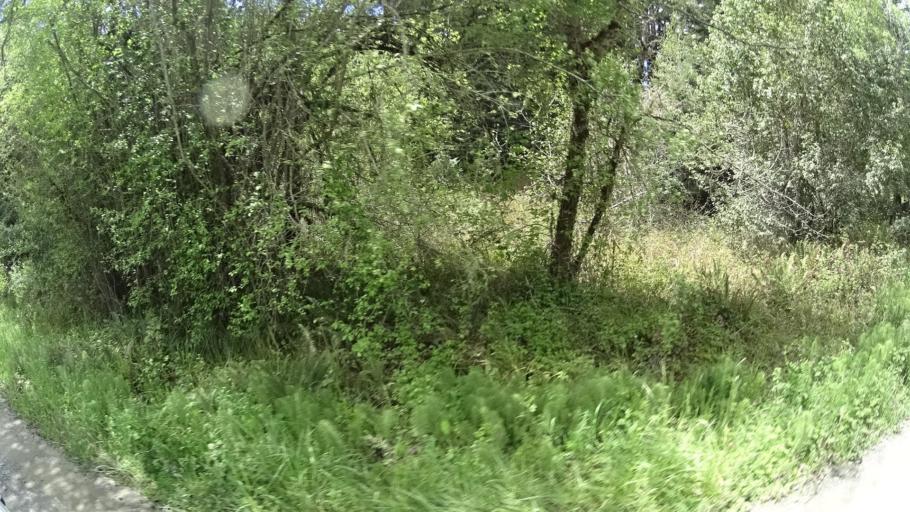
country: US
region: California
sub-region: Humboldt County
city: Blue Lake
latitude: 40.8217
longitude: -123.8920
